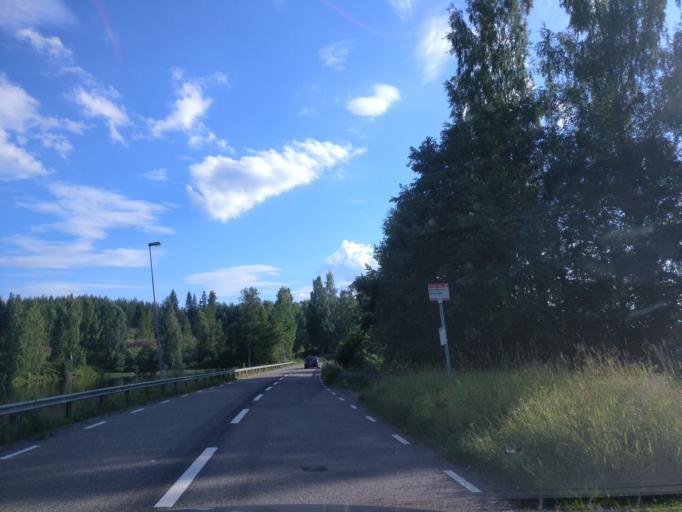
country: SE
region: Dalarna
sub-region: Ludvika Kommun
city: Ludvika
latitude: 60.3012
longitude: 15.2263
